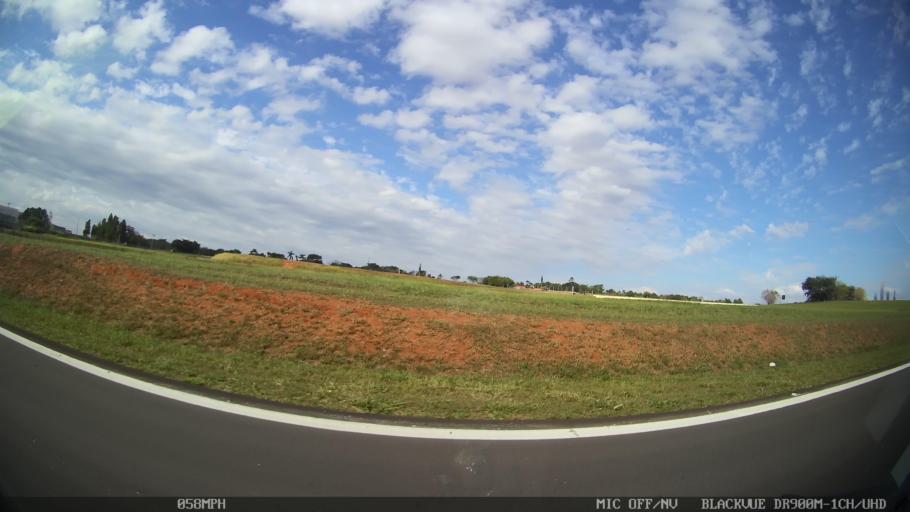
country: BR
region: Sao Paulo
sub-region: Iracemapolis
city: Iracemapolis
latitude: -22.5836
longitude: -47.4593
